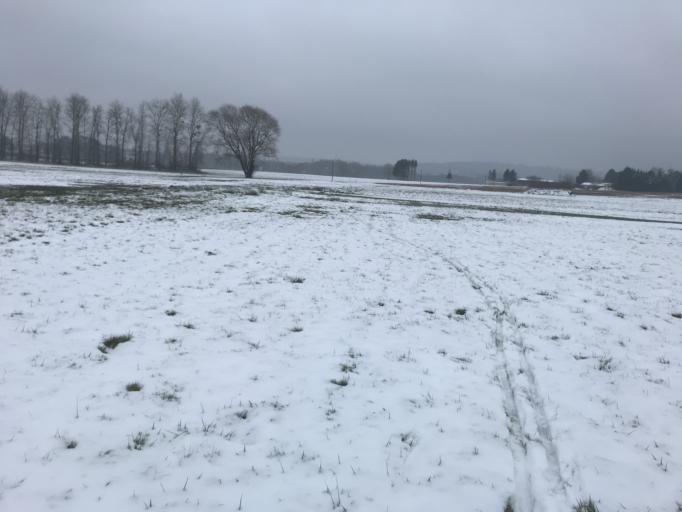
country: FR
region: Lorraine
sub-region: Departement de la Moselle
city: Russange
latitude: 49.4910
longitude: 5.9423
